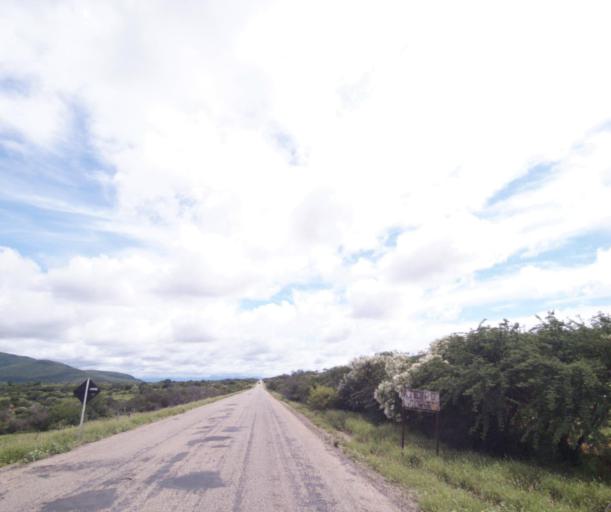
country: BR
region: Bahia
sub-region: Brumado
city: Brumado
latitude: -14.1940
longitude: -41.5805
